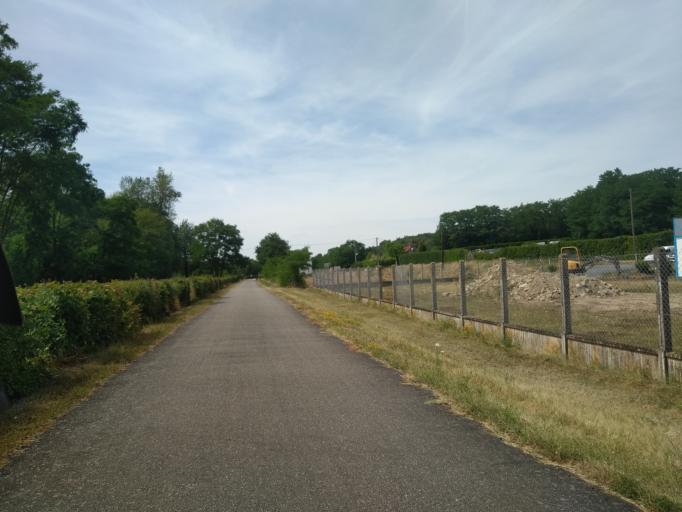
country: FR
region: Auvergne
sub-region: Departement de l'Allier
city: Diou
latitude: 46.5402
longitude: 3.7502
